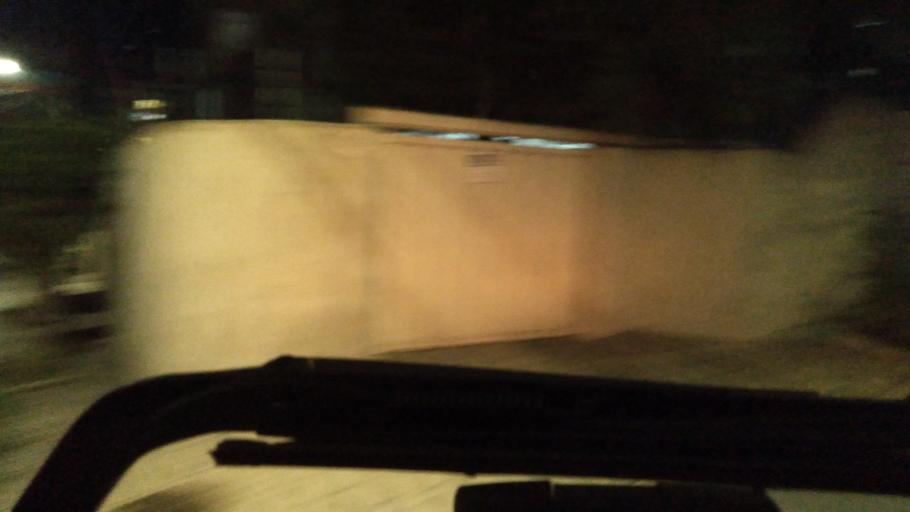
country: BR
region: Minas Gerais
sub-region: Belo Horizonte
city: Belo Horizonte
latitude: -19.9169
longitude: -43.9777
